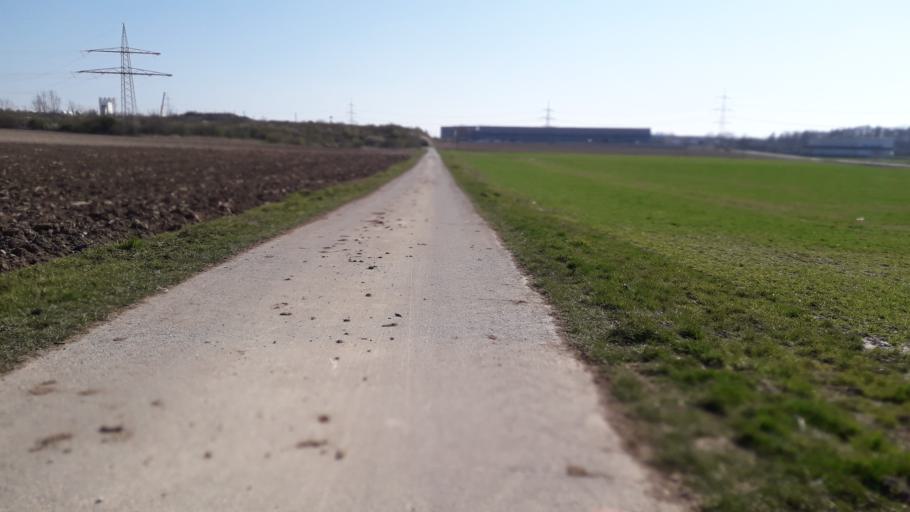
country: DE
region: North Rhine-Westphalia
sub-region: Regierungsbezirk Detmold
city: Paderborn
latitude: 51.6937
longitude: 8.7183
